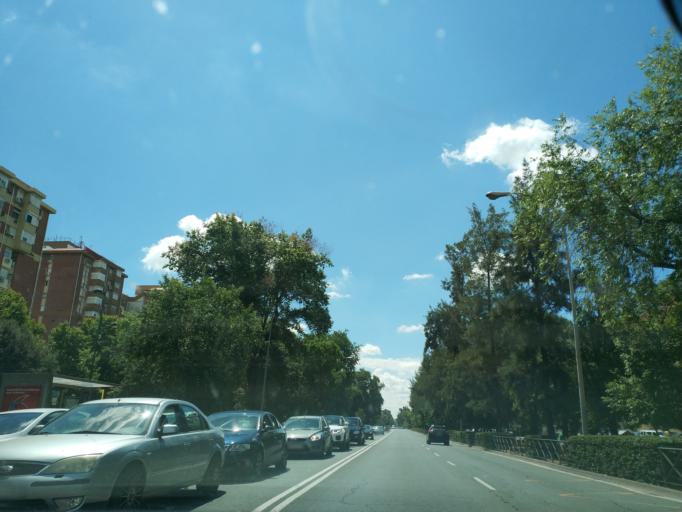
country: ES
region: Andalusia
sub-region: Provincia de Sevilla
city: Sevilla
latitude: 37.3689
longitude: -5.9686
